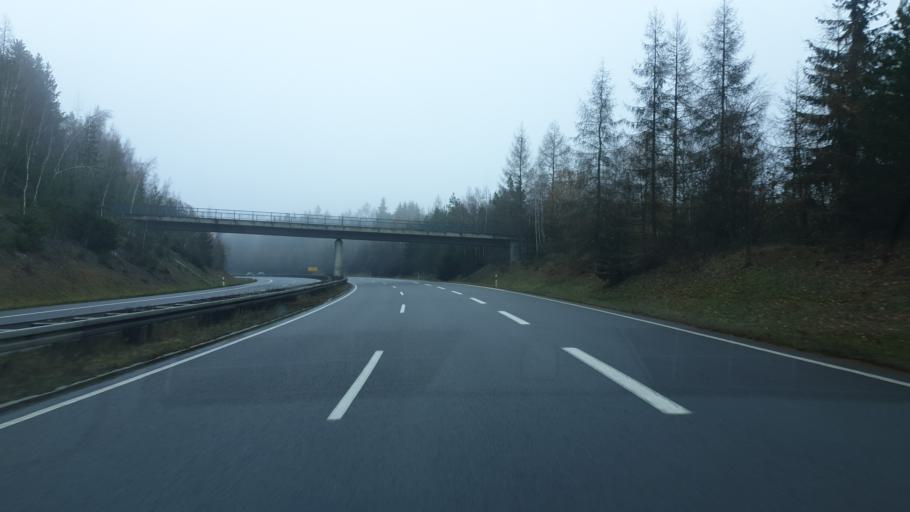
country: DE
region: Saxony
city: Gornau
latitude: 50.7655
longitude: 13.0171
